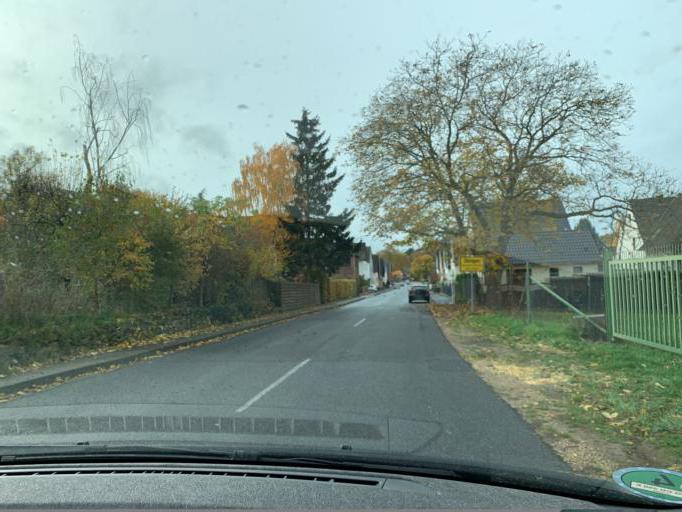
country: DE
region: North Rhine-Westphalia
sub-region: Regierungsbezirk Koln
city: Kreuzau
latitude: 50.7304
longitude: 6.4871
